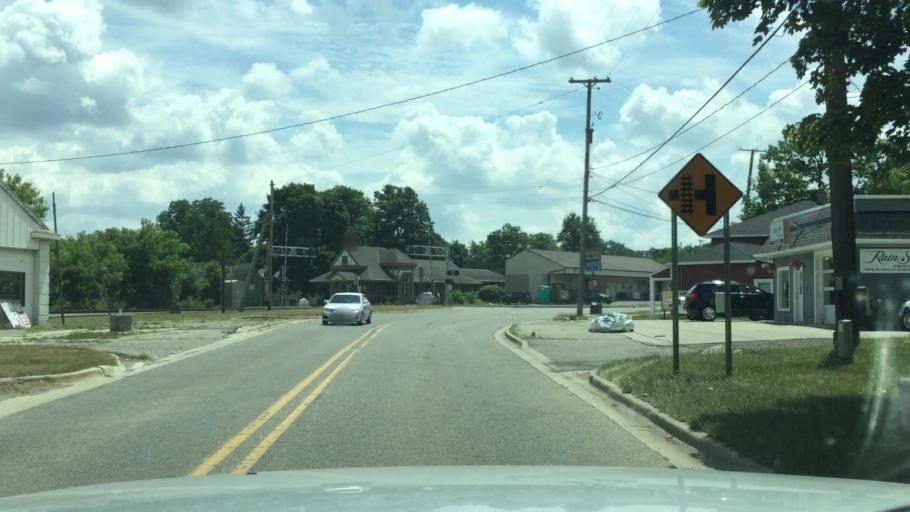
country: US
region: Michigan
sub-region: Genesee County
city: Flushing
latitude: 43.0636
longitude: -83.8630
